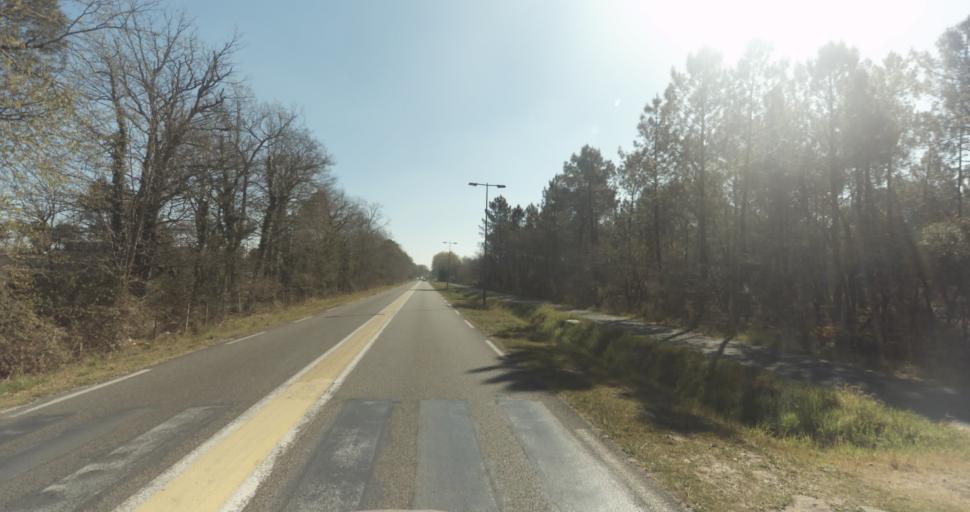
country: FR
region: Aquitaine
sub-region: Departement de la Gironde
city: Martignas-sur-Jalle
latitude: 44.8062
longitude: -0.8007
